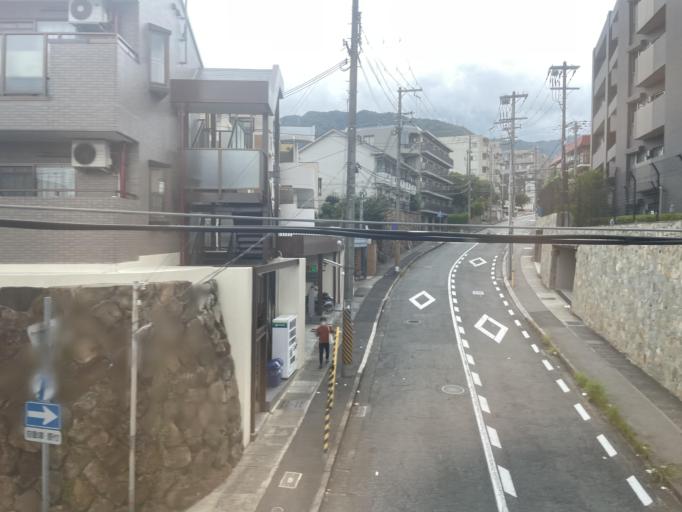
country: JP
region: Hyogo
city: Kobe
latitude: 34.7189
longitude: 135.2323
